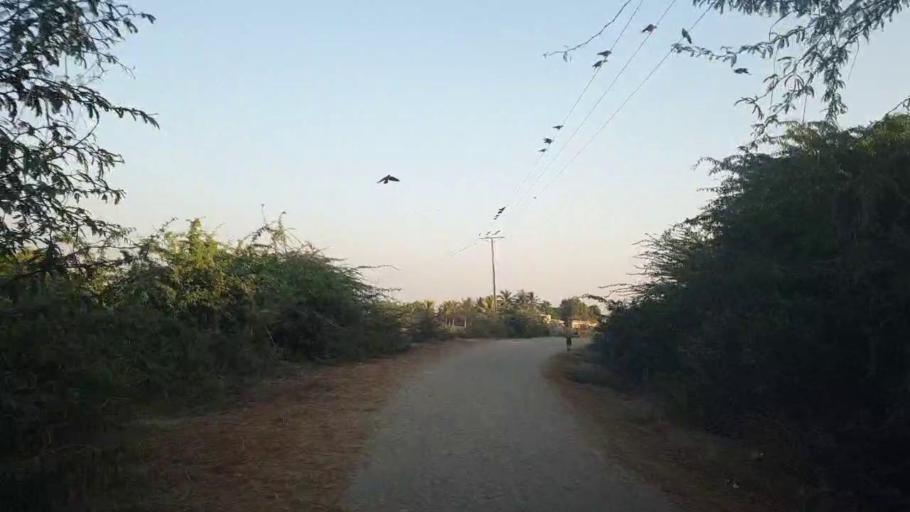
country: PK
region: Sindh
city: Mirpur Sakro
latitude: 24.4626
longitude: 67.5891
